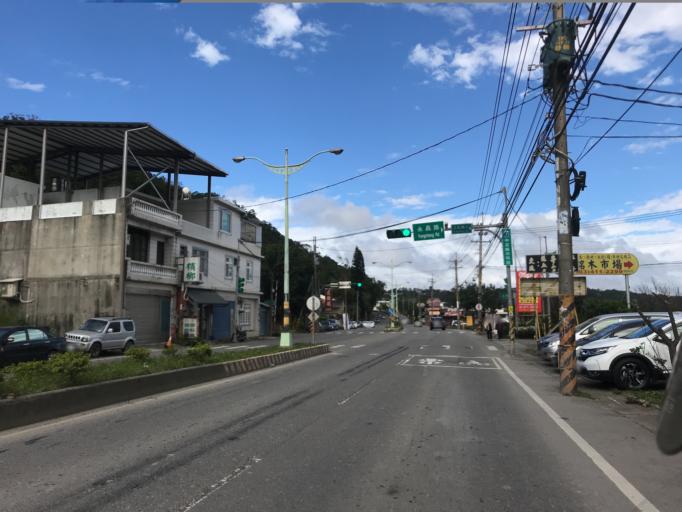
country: TW
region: Taiwan
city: Daxi
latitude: 24.8350
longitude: 121.2460
